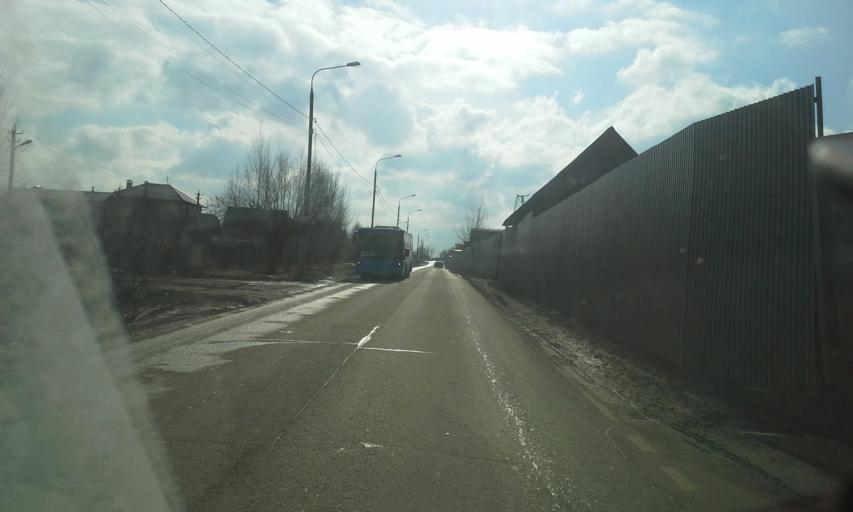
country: RU
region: Moscow
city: Tolstopal'tsevo
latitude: 55.6099
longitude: 37.2003
